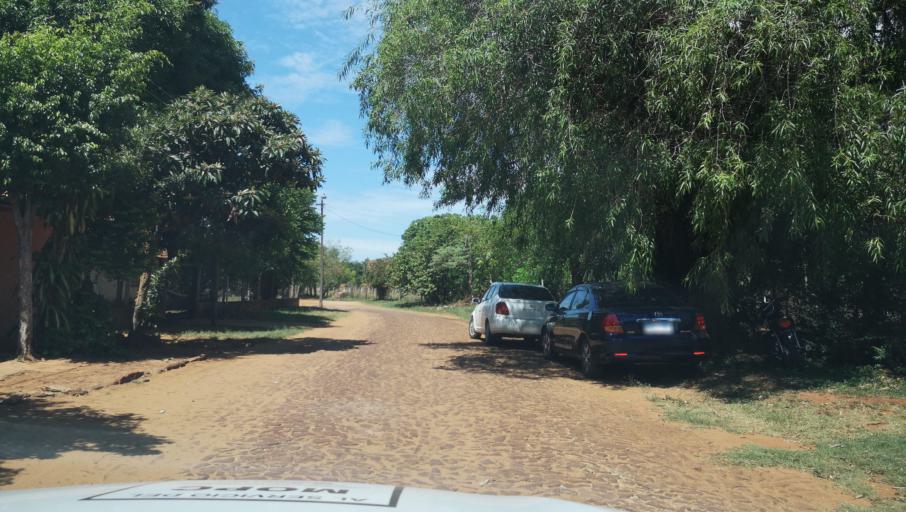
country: PY
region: Misiones
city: Santa Maria
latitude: -26.8981
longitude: -57.0291
